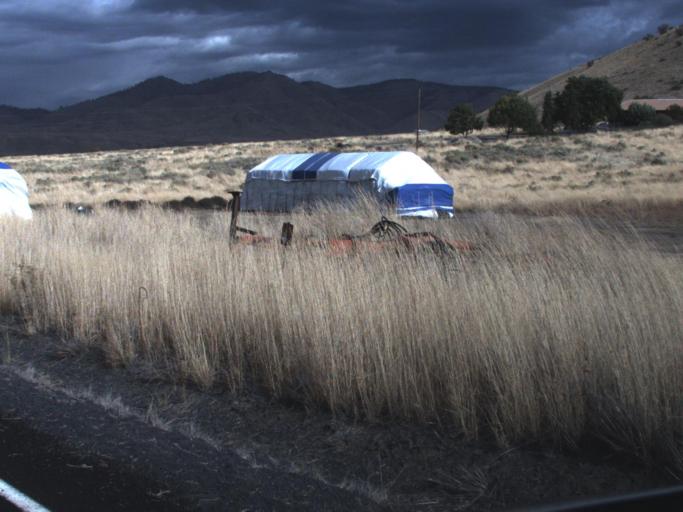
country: US
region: Washington
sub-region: Okanogan County
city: Coulee Dam
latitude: 47.9206
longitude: -118.6894
